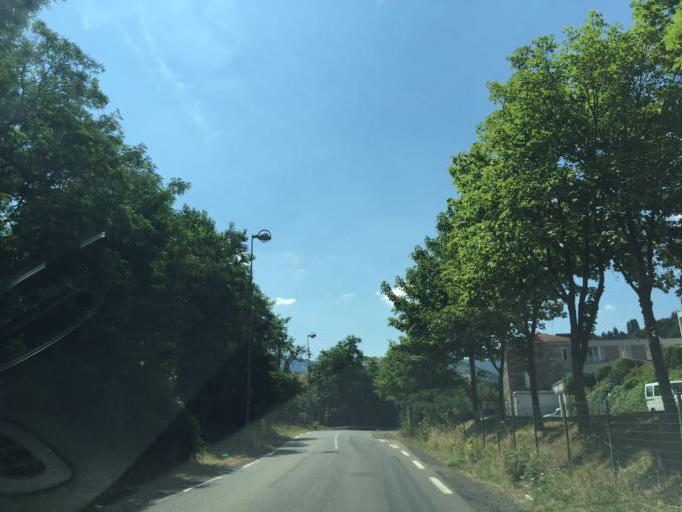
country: FR
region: Rhone-Alpes
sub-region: Departement de la Loire
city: Saint-Chamond
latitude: 45.4417
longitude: 4.5095
